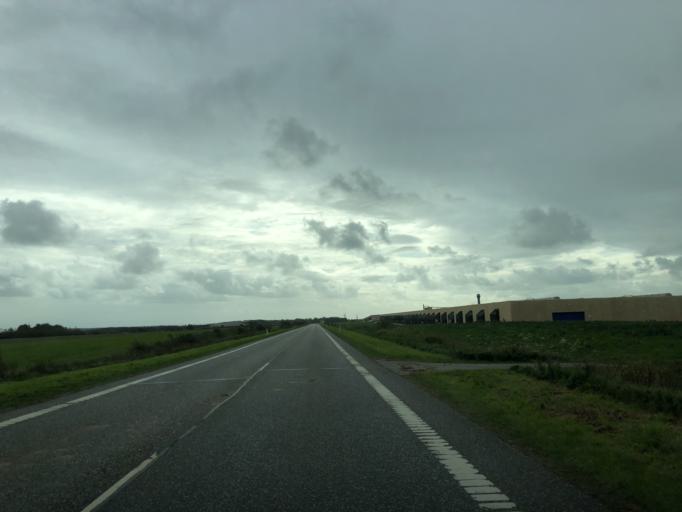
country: DK
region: North Denmark
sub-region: Thisted Kommune
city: Hurup
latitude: 56.7501
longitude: 8.4449
